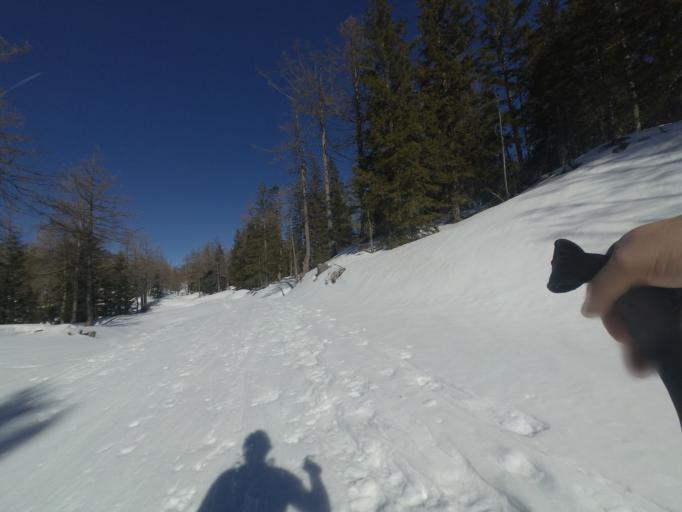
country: AT
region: Upper Austria
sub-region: Politischer Bezirk Gmunden
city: Sankt Wolfgang im Salzkammergut
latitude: 47.6619
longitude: 13.3866
